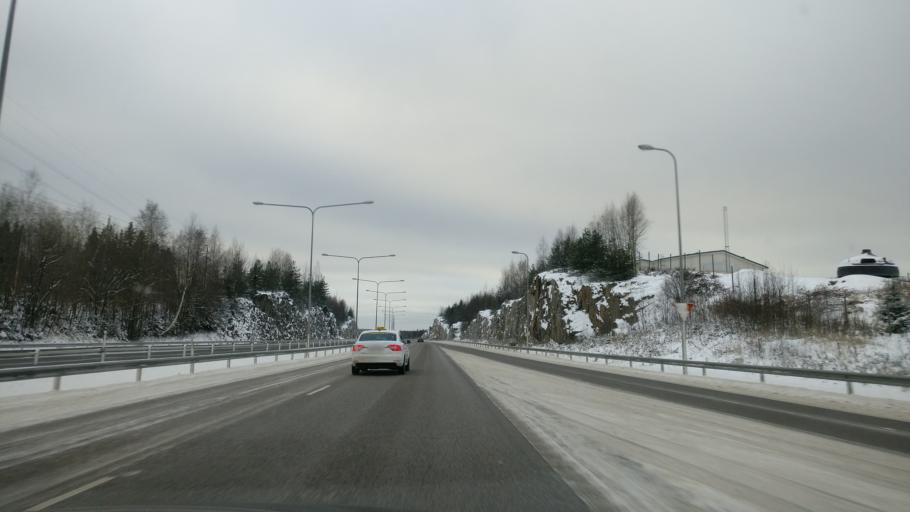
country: FI
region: Paijanne Tavastia
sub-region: Lahti
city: Lahti
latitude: 60.9664
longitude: 25.7109
